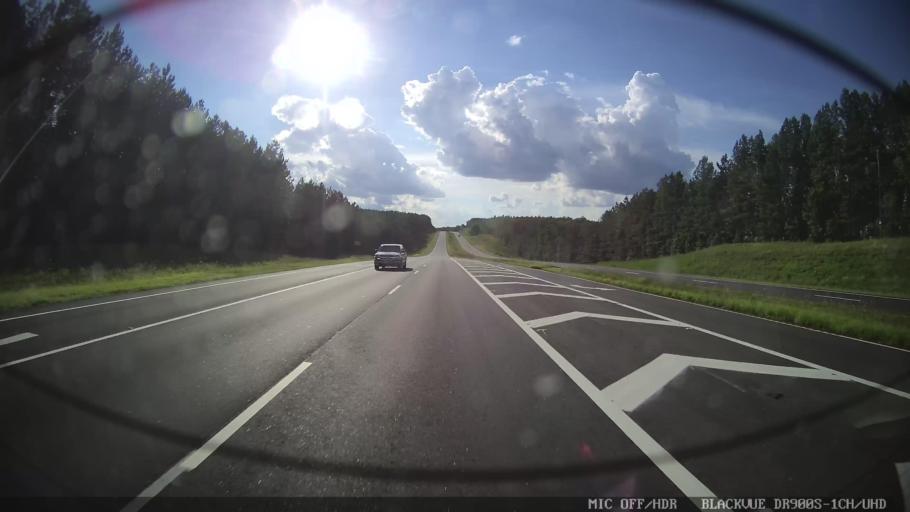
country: US
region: Georgia
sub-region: Floyd County
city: Lindale
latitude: 34.2100
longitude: -85.0944
